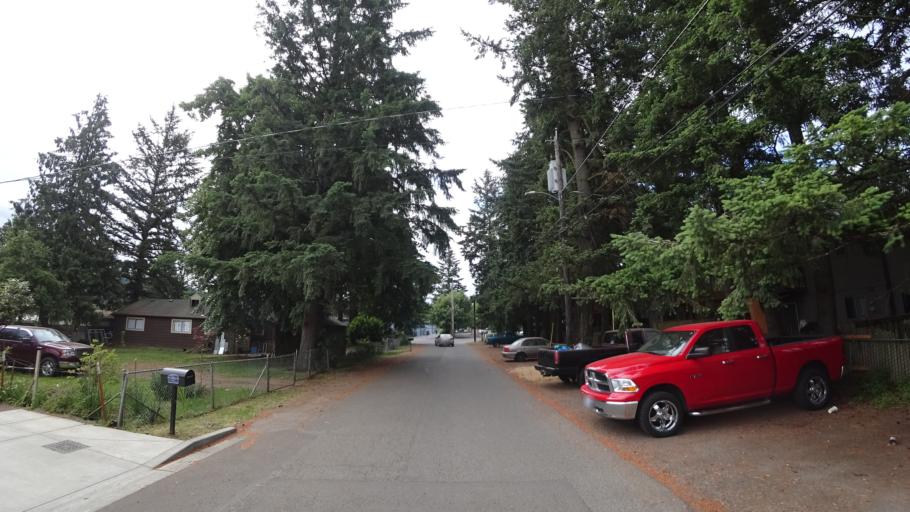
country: US
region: Oregon
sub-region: Multnomah County
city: Lents
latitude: 45.4981
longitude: -122.5285
